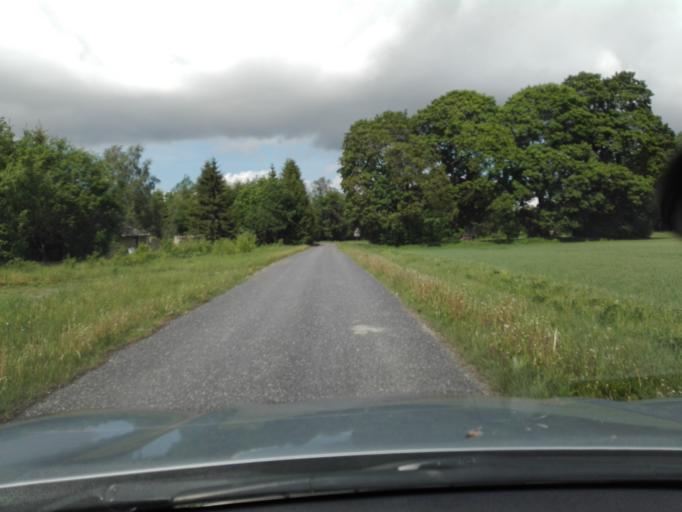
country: EE
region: Raplamaa
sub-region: Kehtna vald
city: Kehtna
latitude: 58.9603
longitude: 24.8953
